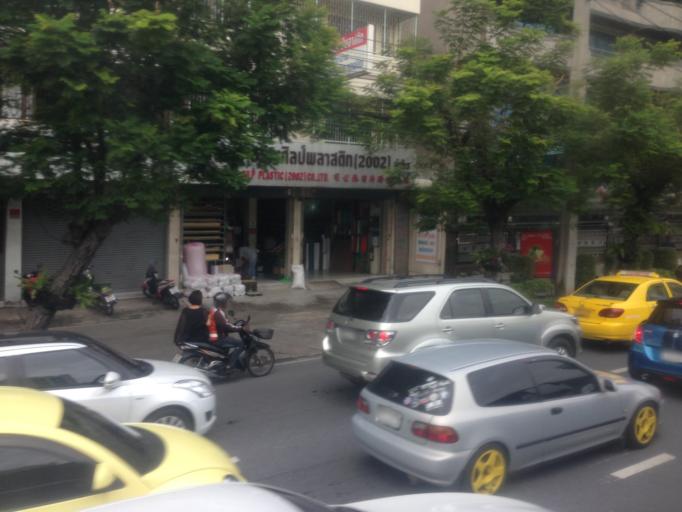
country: TH
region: Bangkok
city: Sathon
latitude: 13.7152
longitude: 100.5334
